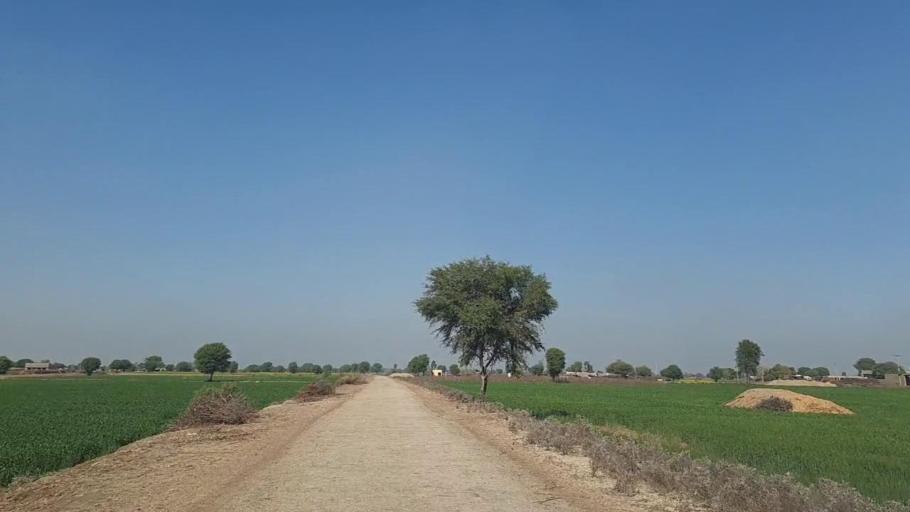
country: PK
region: Sindh
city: Shahpur Chakar
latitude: 26.1978
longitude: 68.5663
